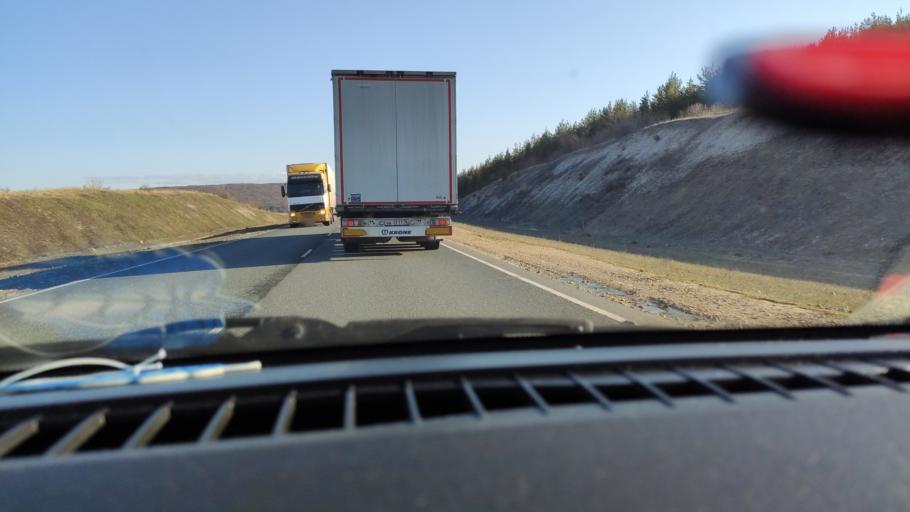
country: RU
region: Saratov
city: Alekseyevka
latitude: 52.3856
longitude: 47.9742
